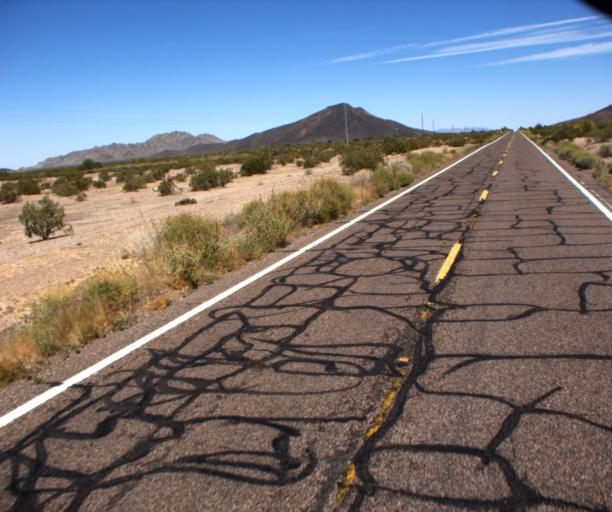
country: US
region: Arizona
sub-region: Maricopa County
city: Gila Bend
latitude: 32.7349
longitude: -112.8334
